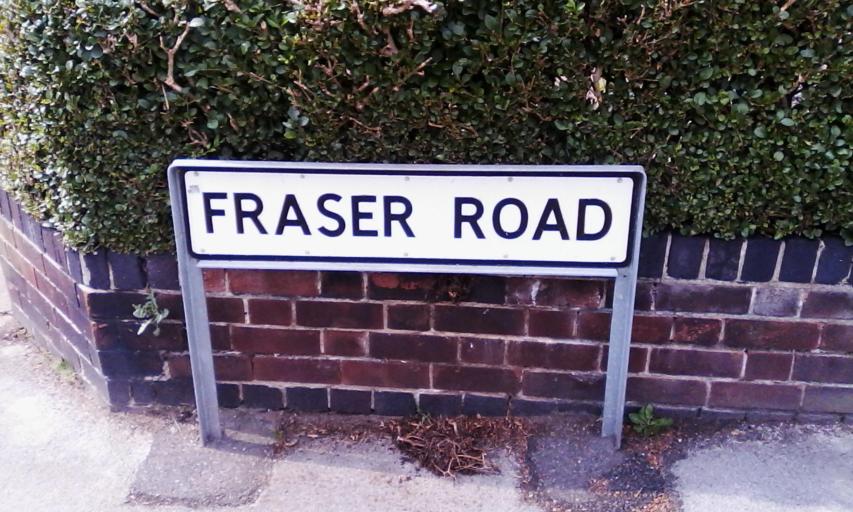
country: GB
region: England
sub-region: Nottinghamshire
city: Arnold
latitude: 52.9734
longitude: -1.1083
